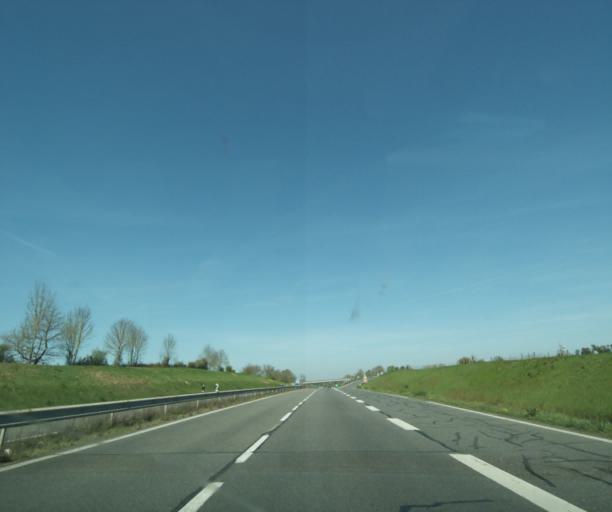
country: FR
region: Bourgogne
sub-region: Departement de la Nievre
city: Saint-Pierre-le-Moutier
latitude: 46.7823
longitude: 3.1283
